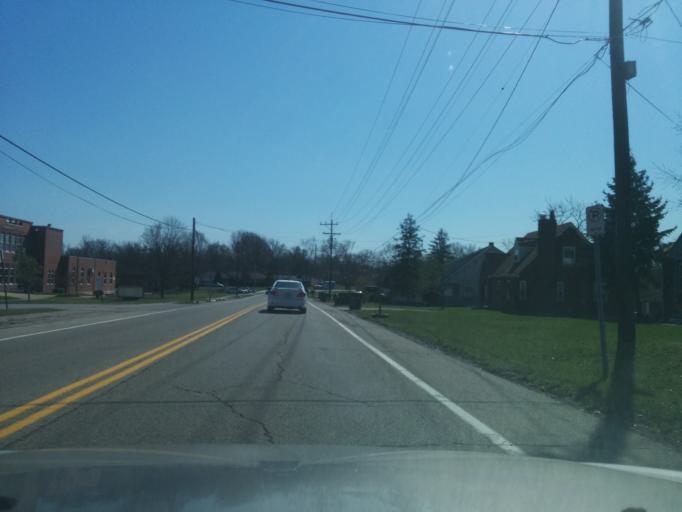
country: US
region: Ohio
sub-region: Hamilton County
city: Dry Ridge
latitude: 39.2392
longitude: -84.6147
